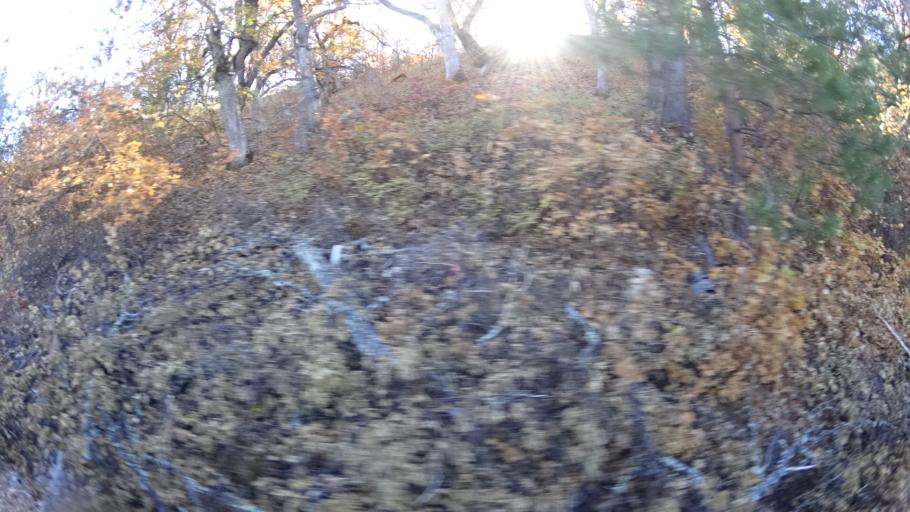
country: US
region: California
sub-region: Siskiyou County
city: Yreka
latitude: 41.8414
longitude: -122.8889
